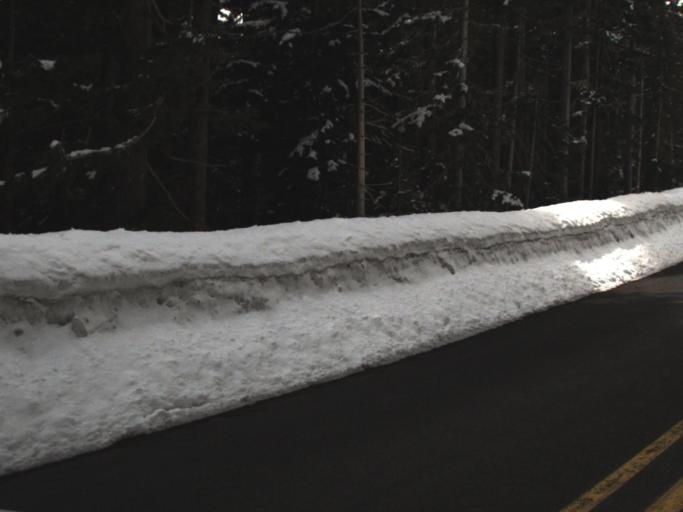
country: US
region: Washington
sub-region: Kittitas County
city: Cle Elum
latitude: 46.9131
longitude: -121.4090
